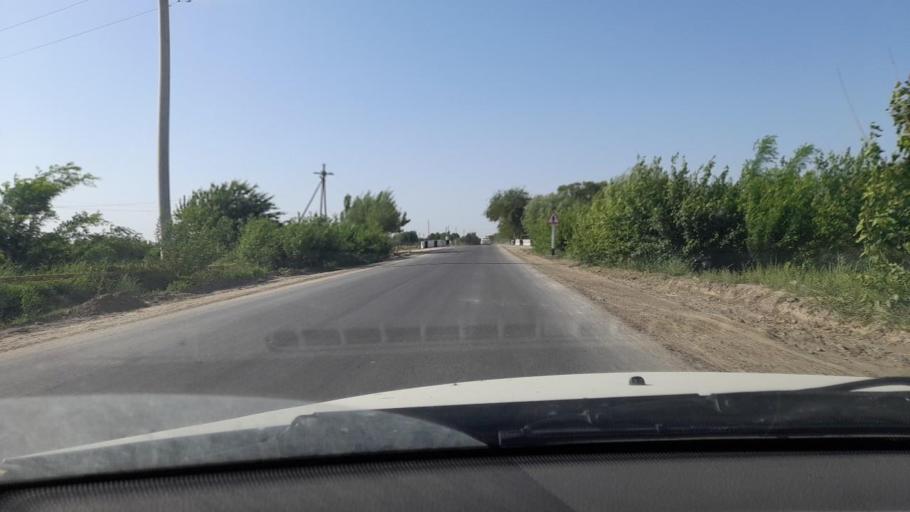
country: UZ
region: Bukhara
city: Romiton
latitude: 40.0654
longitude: 64.3271
